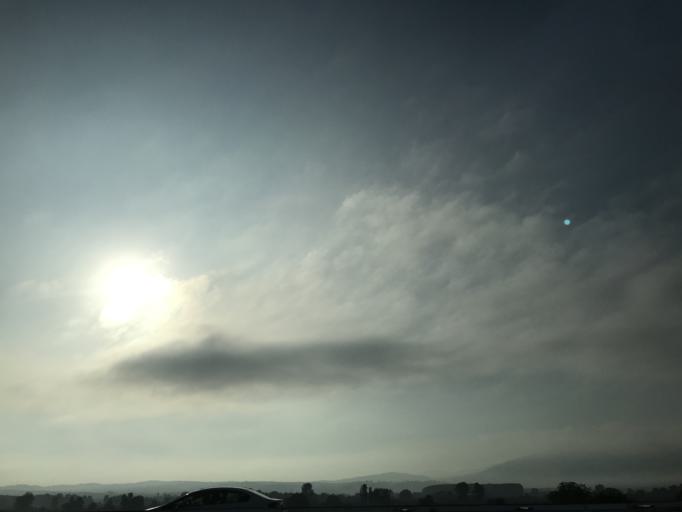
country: TR
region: Balikesir
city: Gobel
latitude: 40.0031
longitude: 28.1941
